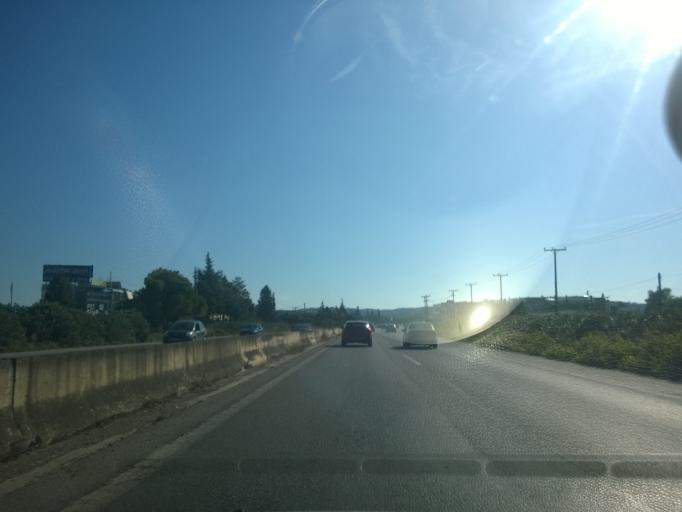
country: GR
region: Central Macedonia
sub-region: Nomos Thessalonikis
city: Neo Rysi
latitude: 40.5026
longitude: 23.0055
